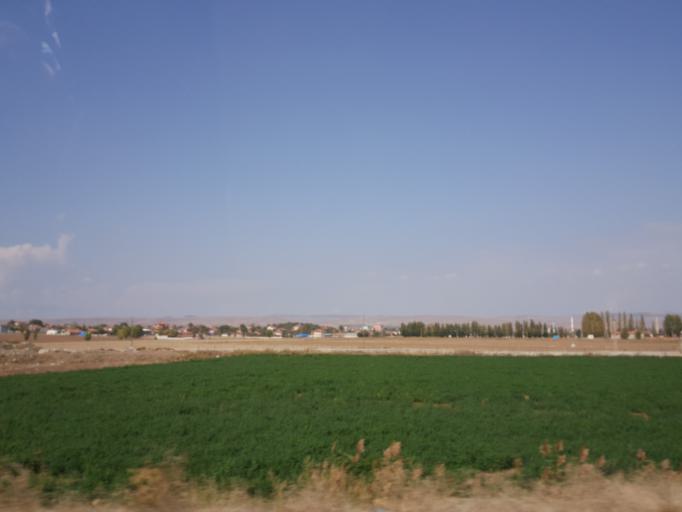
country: TR
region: Corum
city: Alaca
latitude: 40.1505
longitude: 34.8473
